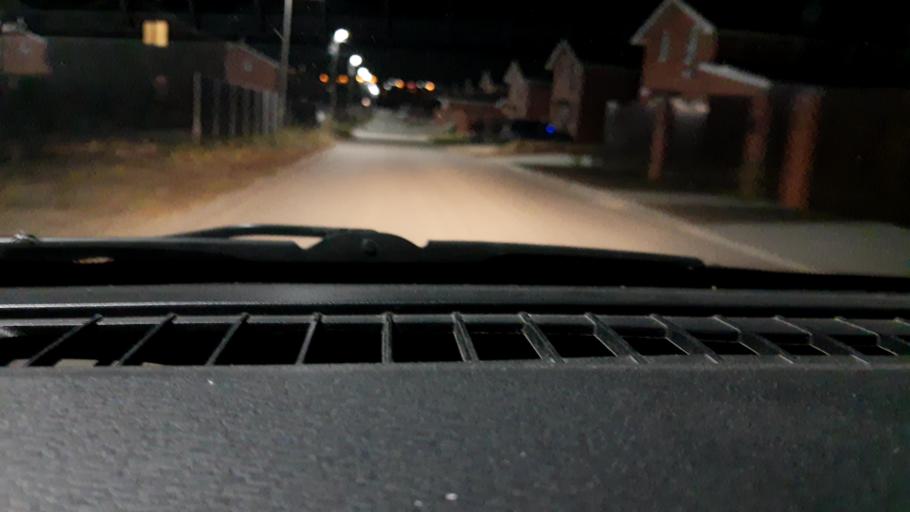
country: RU
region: Nizjnij Novgorod
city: Afonino
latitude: 56.2082
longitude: 44.1318
